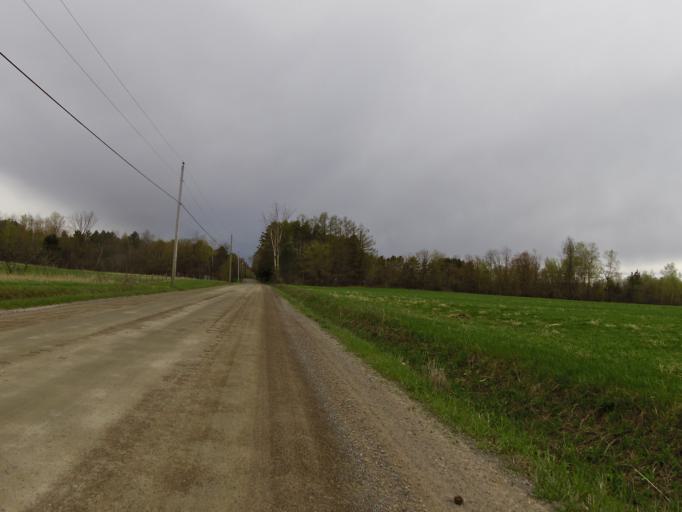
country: CA
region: Ontario
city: Hawkesbury
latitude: 45.6194
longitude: -74.5415
